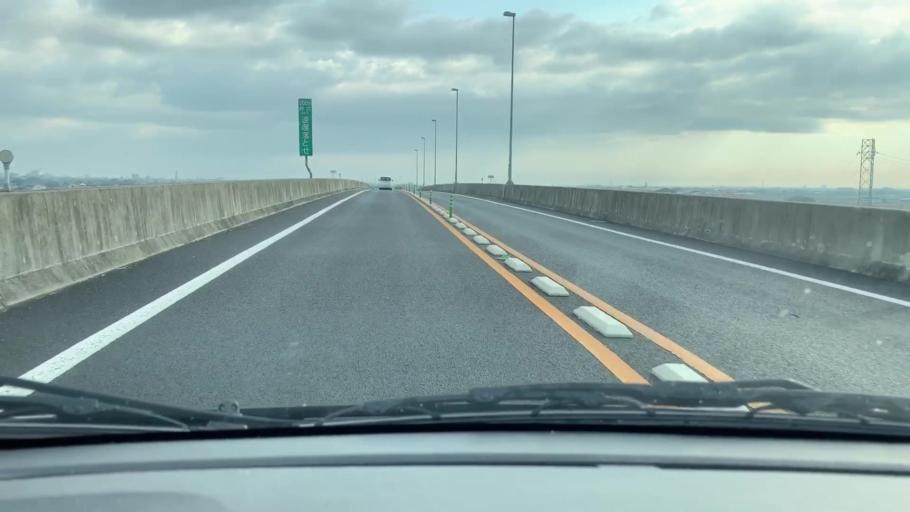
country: JP
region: Saga Prefecture
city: Saga-shi
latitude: 33.2315
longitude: 130.2487
